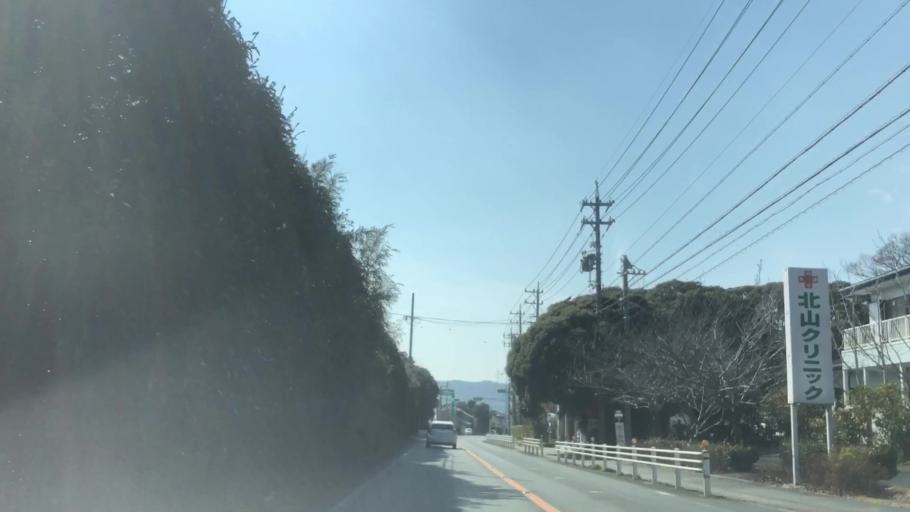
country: JP
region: Aichi
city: Tahara
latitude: 34.6573
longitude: 137.2469
